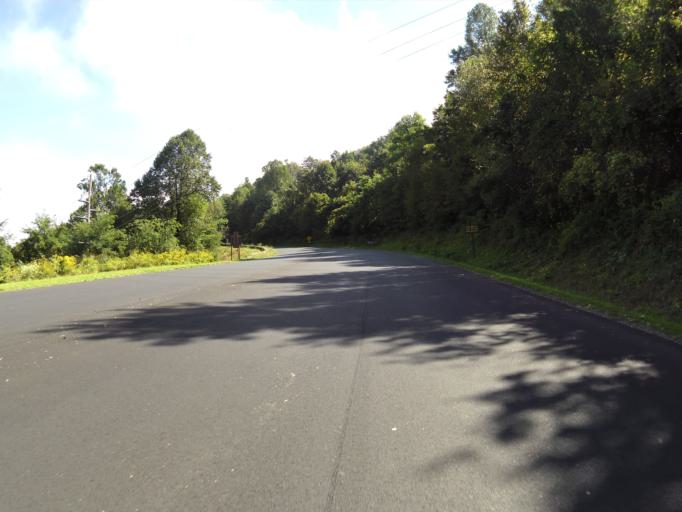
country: US
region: Virginia
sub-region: Page County
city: Luray
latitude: 38.6595
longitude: -78.3194
